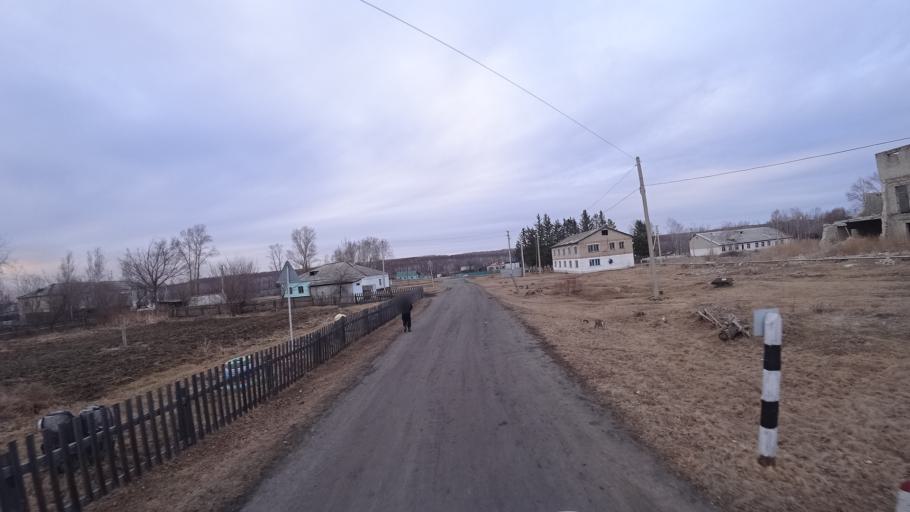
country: RU
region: Amur
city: Bureya
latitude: 50.0185
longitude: 129.7704
